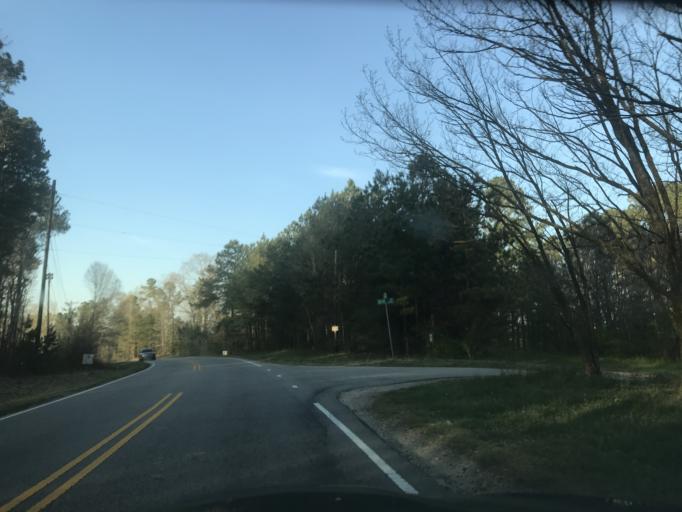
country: US
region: North Carolina
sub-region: Wake County
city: Knightdale
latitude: 35.7466
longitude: -78.5349
